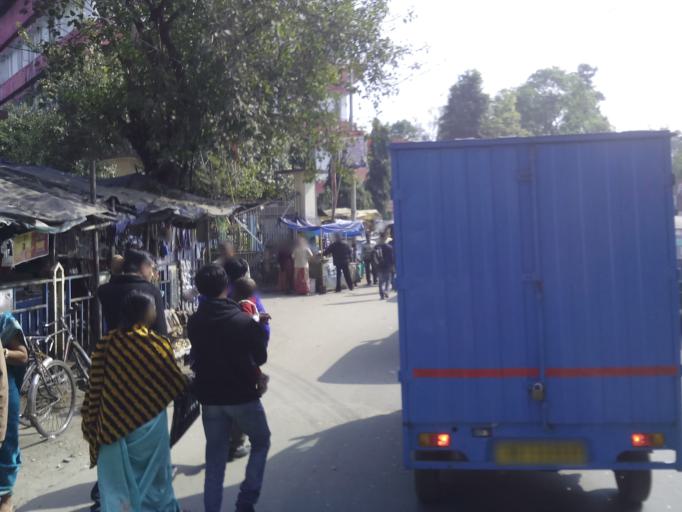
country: IN
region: West Bengal
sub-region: Darjiling
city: Shiliguri
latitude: 26.7099
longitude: 88.4283
